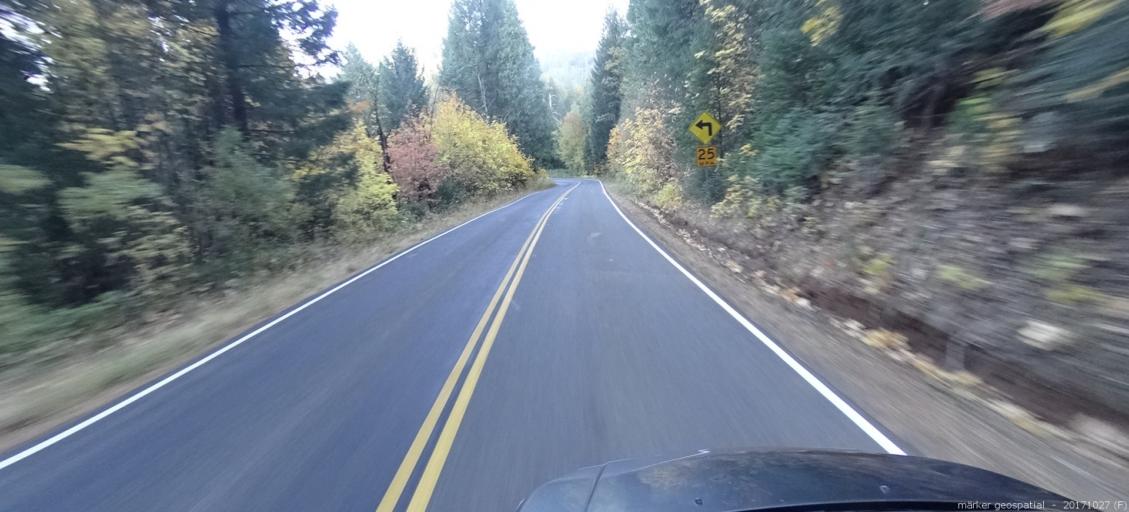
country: US
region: California
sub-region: Shasta County
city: Burney
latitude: 40.8993
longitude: -121.9011
